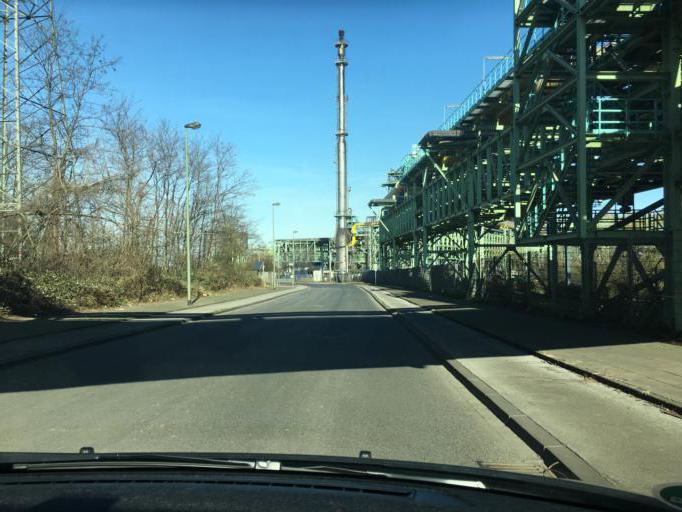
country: DE
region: North Rhine-Westphalia
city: Meiderich
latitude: 51.4980
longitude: 6.7281
